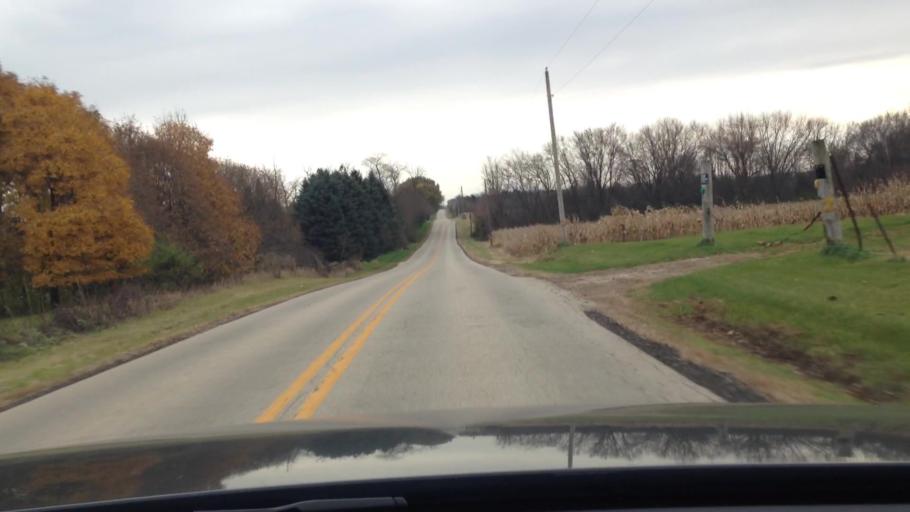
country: US
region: Illinois
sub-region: McHenry County
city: Woodstock
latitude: 42.2883
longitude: -88.4770
